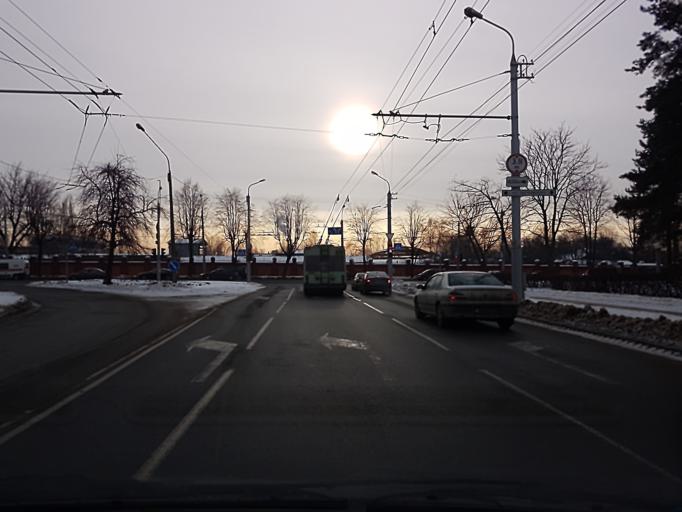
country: BY
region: Minsk
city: Minsk
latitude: 53.8810
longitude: 27.5208
